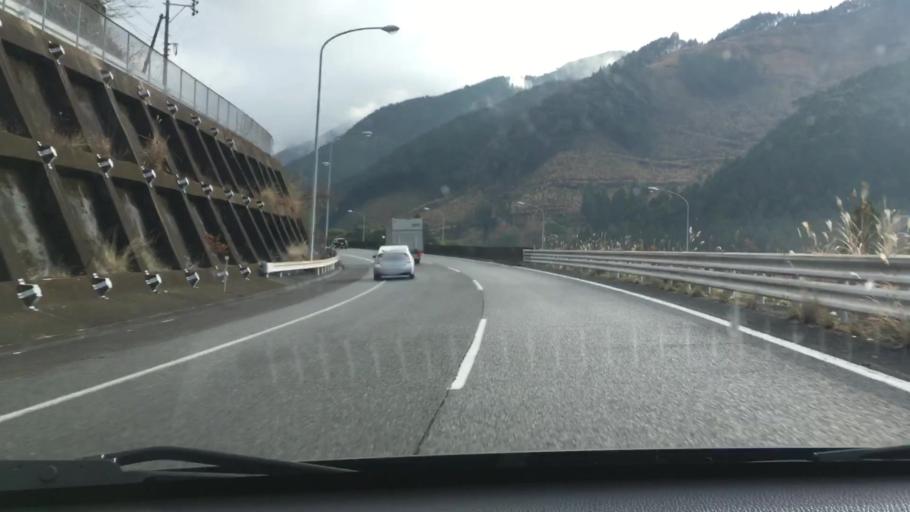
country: JP
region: Kumamoto
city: Yatsushiro
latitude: 32.4031
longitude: 130.6977
